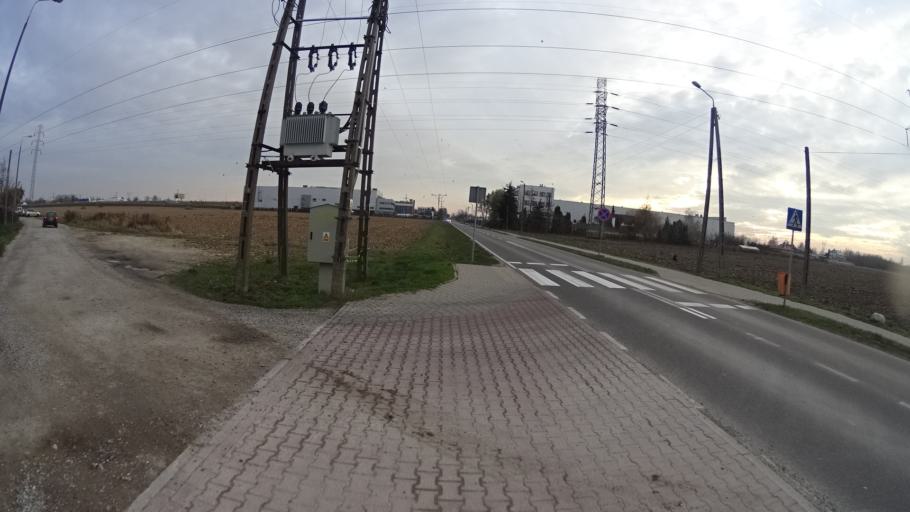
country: PL
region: Masovian Voivodeship
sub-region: Powiat warszawski zachodni
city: Babice
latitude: 52.2211
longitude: 20.8600
